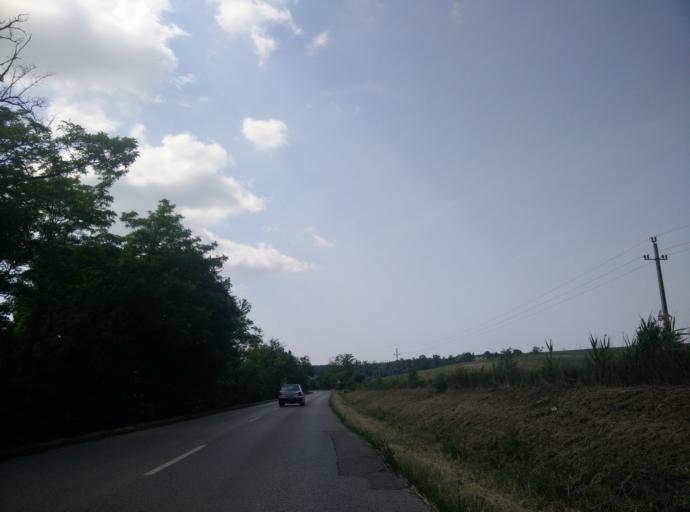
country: HU
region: Pest
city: Biatorbagy
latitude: 47.4757
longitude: 18.7935
